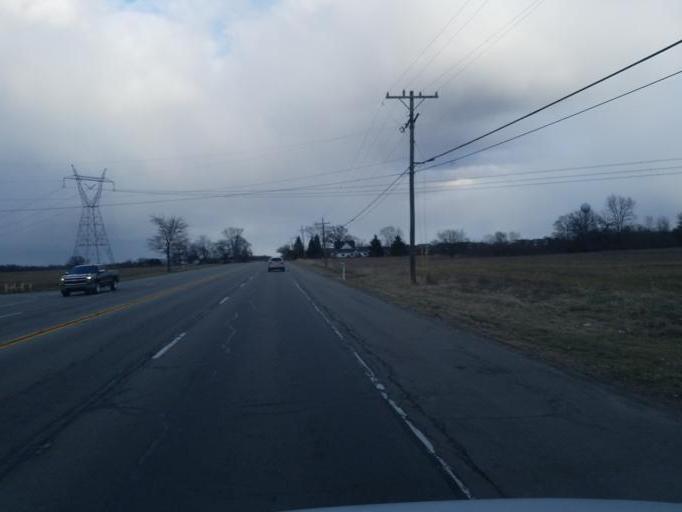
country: US
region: Indiana
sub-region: Hancock County
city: New Palestine
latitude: 39.7796
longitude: -85.8924
